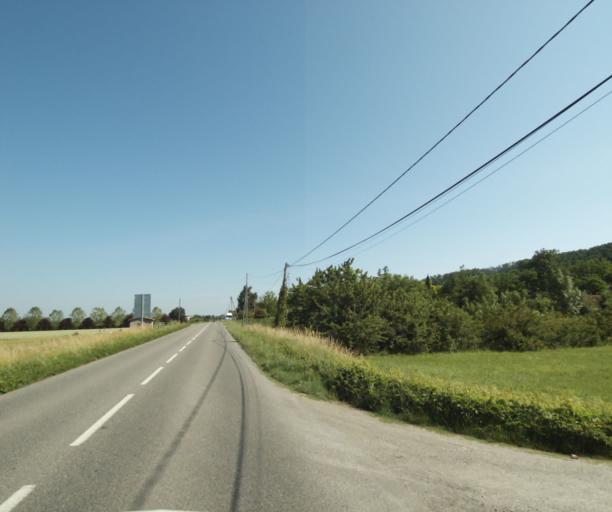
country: FR
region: Midi-Pyrenees
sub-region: Departement du Tarn-et-Garonne
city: Bressols
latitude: 43.9767
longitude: 1.3569
